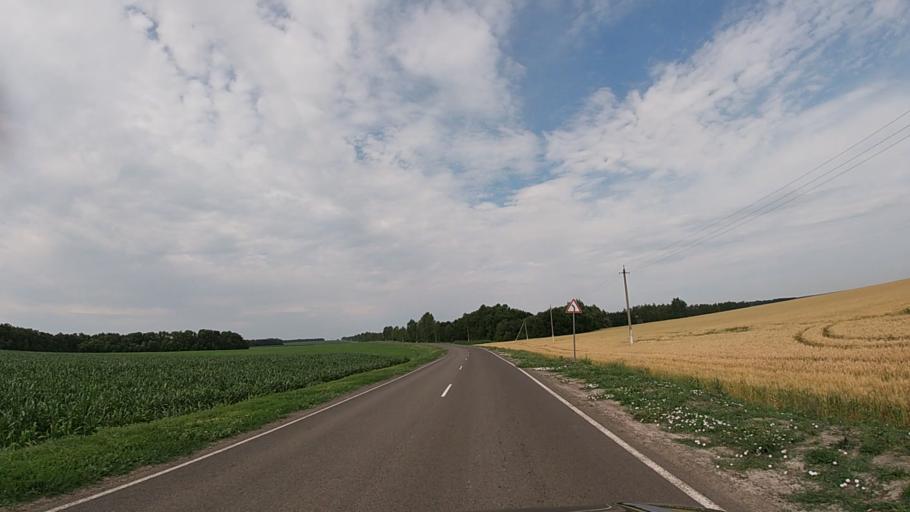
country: RU
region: Belgorod
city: Krasnaya Yaruga
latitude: 50.8329
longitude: 35.4854
